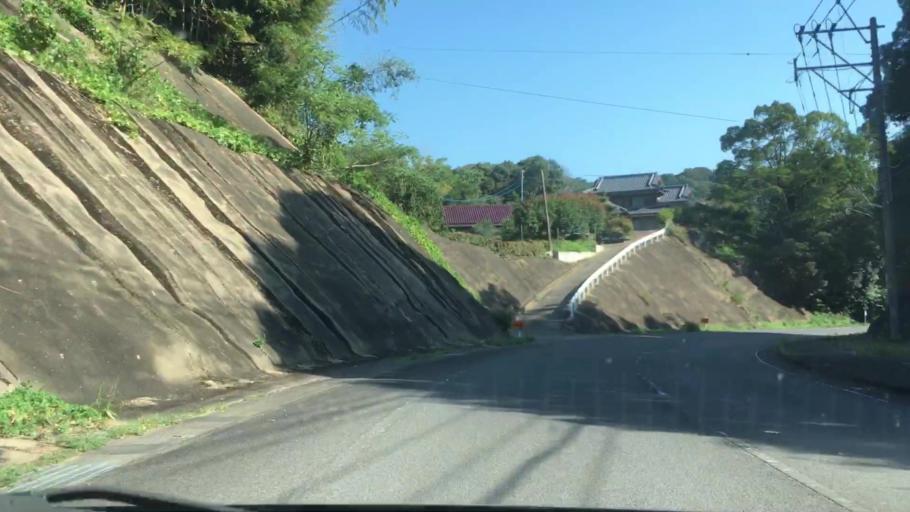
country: JP
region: Nagasaki
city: Sasebo
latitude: 32.9988
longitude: 129.6592
